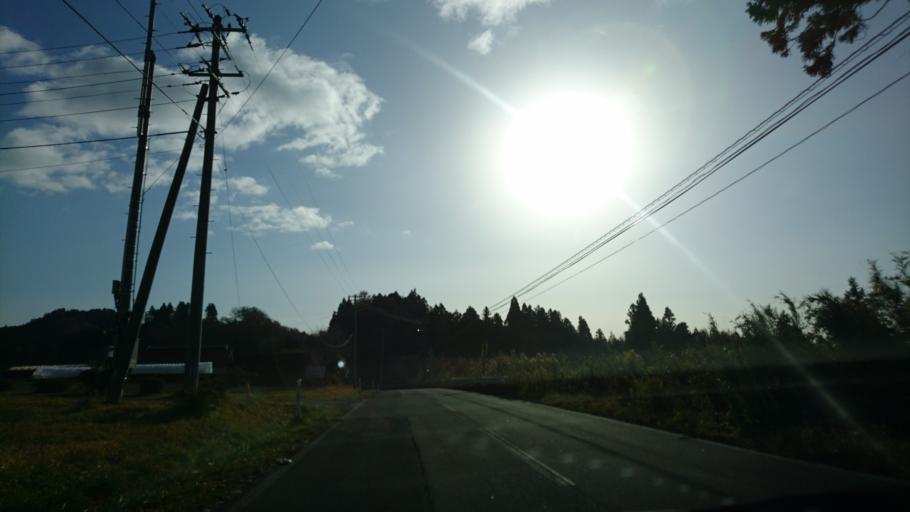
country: JP
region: Iwate
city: Ichinoseki
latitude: 38.8754
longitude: 141.2934
